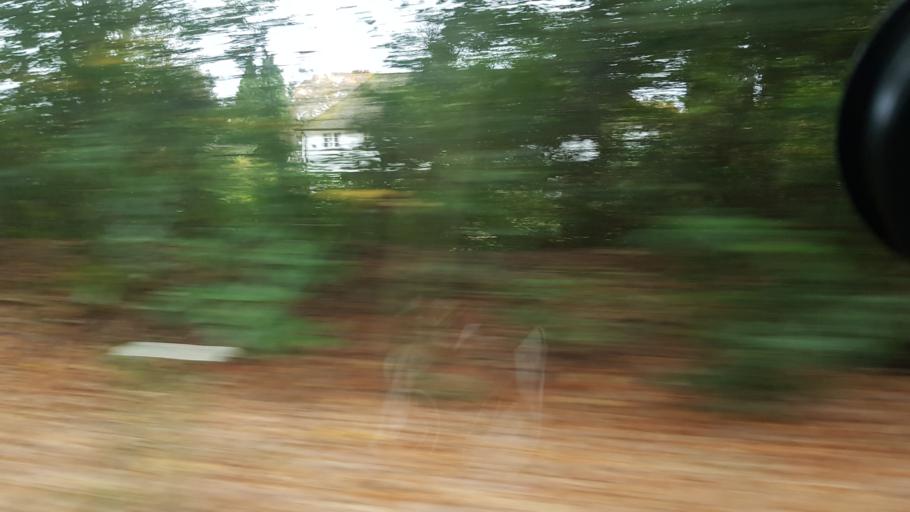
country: GB
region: England
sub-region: Hampshire
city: Eversley
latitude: 51.3599
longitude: -0.8782
